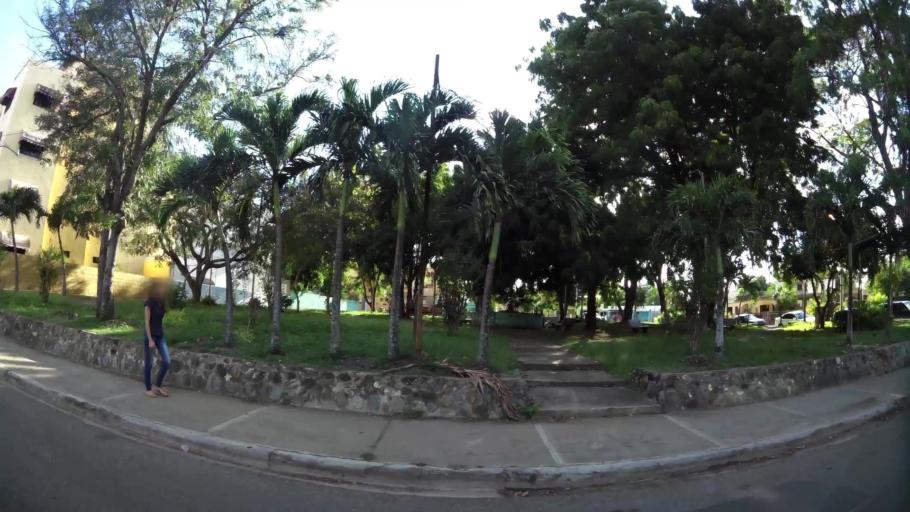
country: DO
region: Santiago
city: Santiago de los Caballeros
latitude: 19.4627
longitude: -70.6957
